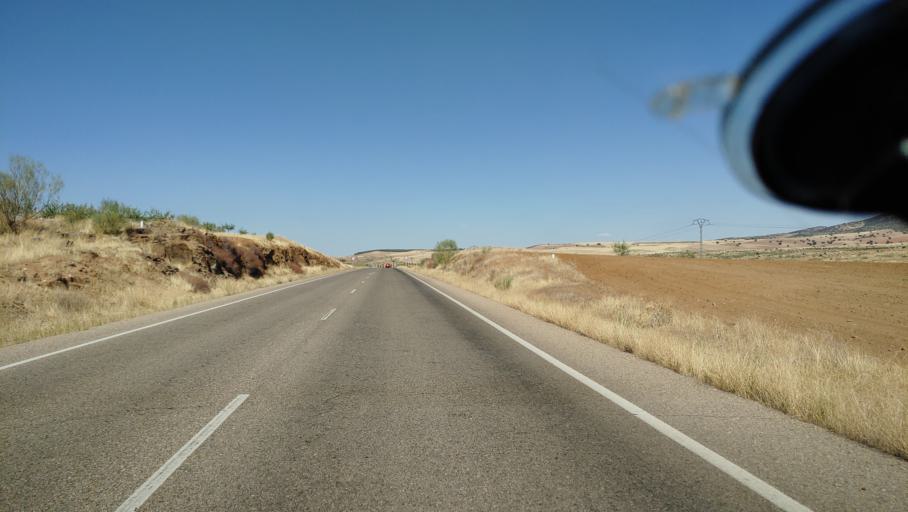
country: ES
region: Castille-La Mancha
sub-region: Province of Toledo
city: Casasbuenas
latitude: 39.7367
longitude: -4.1021
